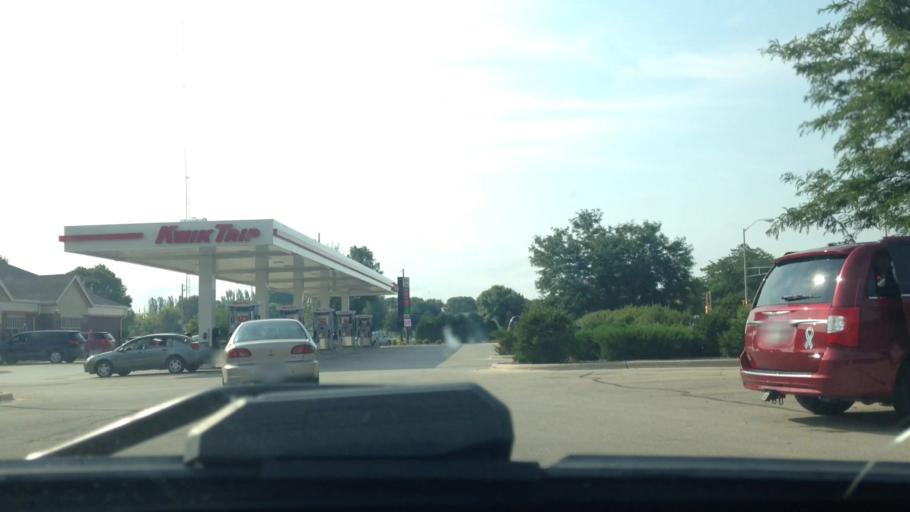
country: US
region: Wisconsin
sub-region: Fond du Lac County
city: North Fond du Lac
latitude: 43.7927
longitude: -88.4732
